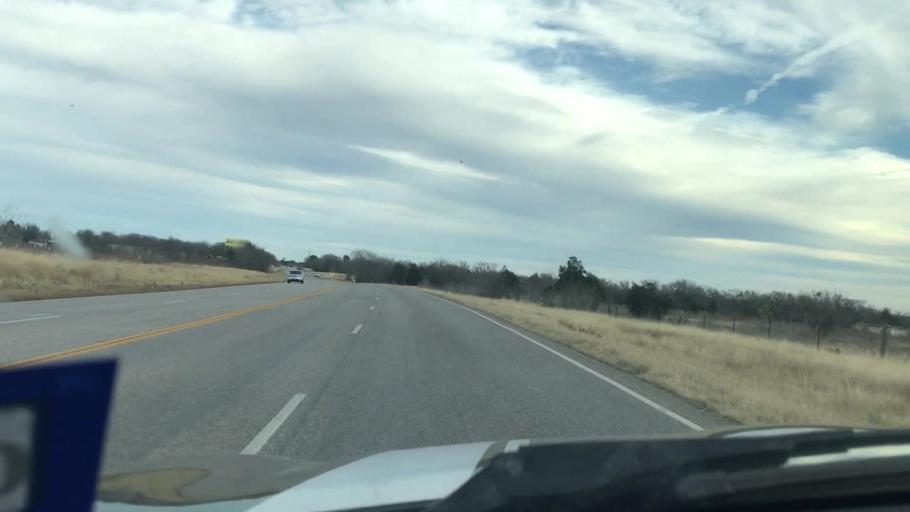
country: US
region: Texas
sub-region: Bastrop County
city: Elgin
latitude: 30.2969
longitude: -97.2813
